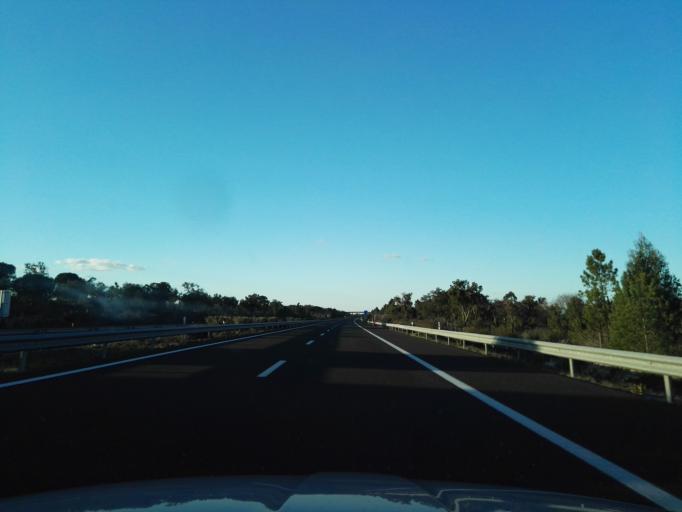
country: PT
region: Santarem
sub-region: Benavente
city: Poceirao
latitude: 38.8186
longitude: -8.7115
